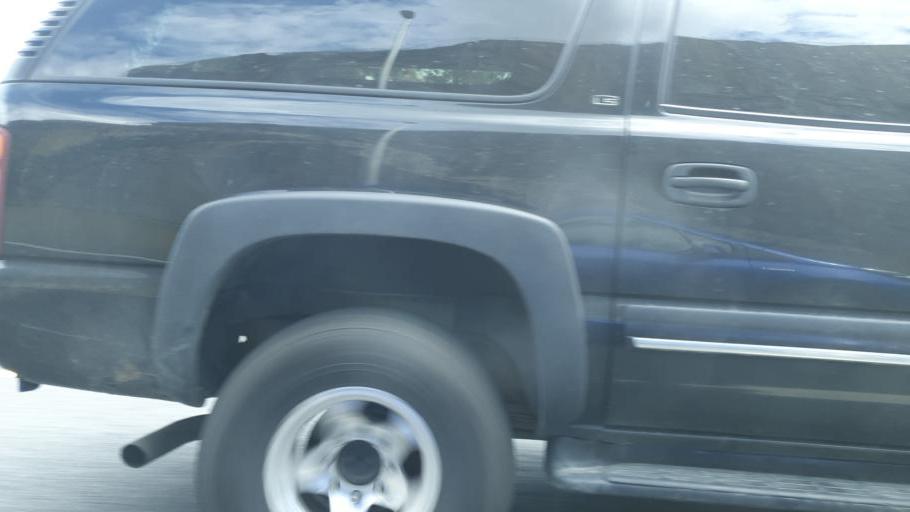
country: NO
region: Sor-Trondelag
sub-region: Midtre Gauldal
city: Storen
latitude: 62.9349
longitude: 10.1867
